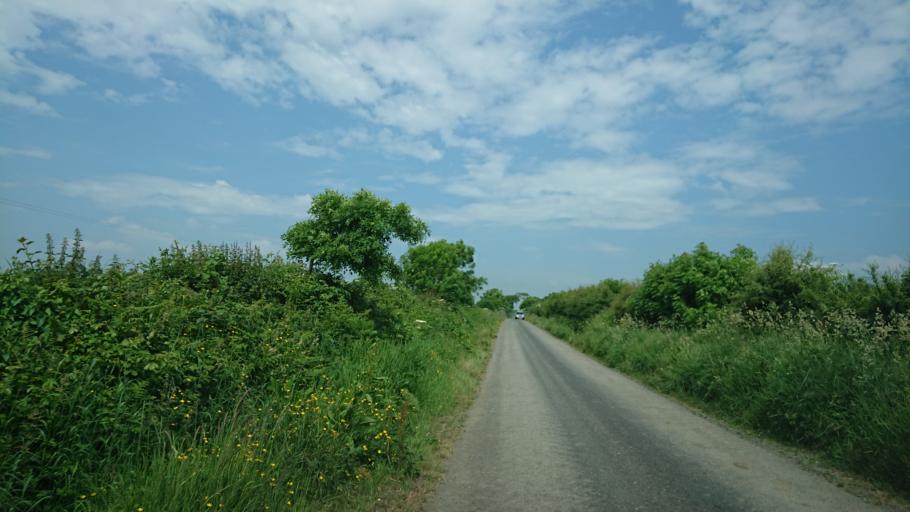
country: IE
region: Munster
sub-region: Waterford
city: Dunmore East
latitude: 52.2178
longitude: -6.9999
